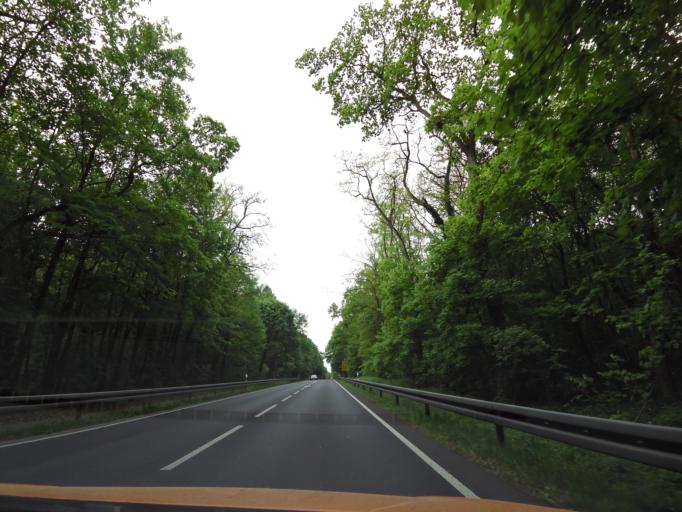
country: DE
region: Brandenburg
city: Michendorf
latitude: 52.2811
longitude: 13.0100
